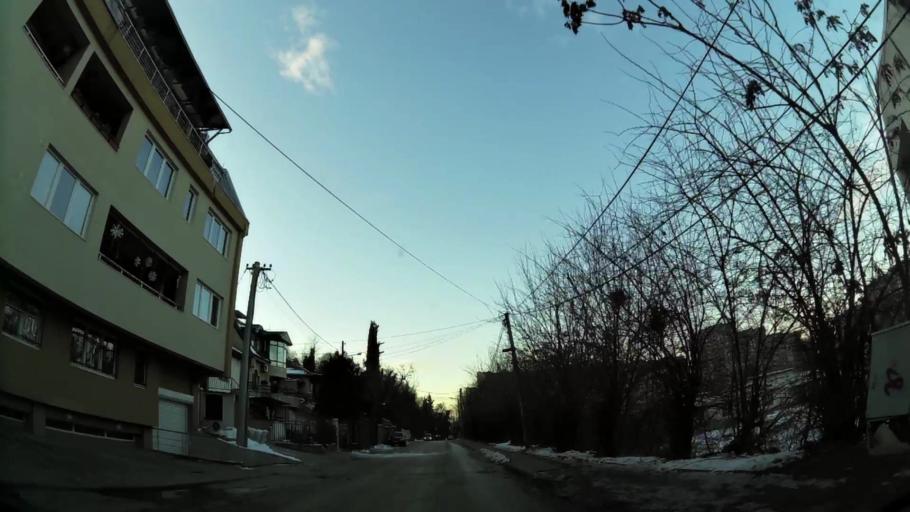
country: MK
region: Karpos
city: Skopje
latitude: 41.9910
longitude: 21.4131
